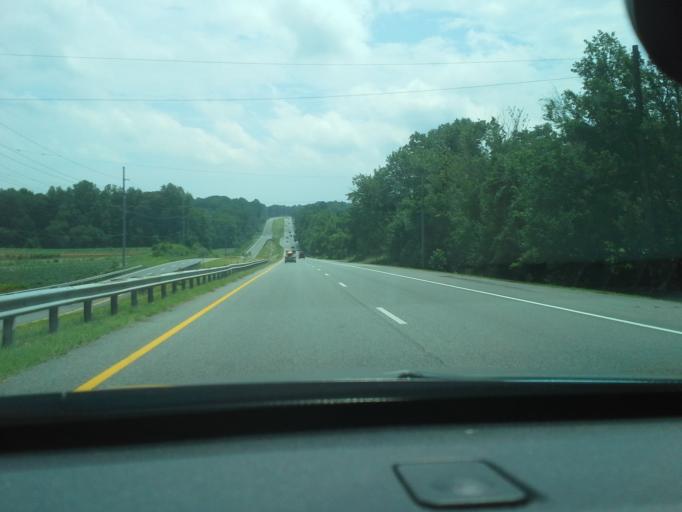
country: US
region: Maryland
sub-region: Calvert County
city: Owings
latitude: 38.6713
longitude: -76.6200
